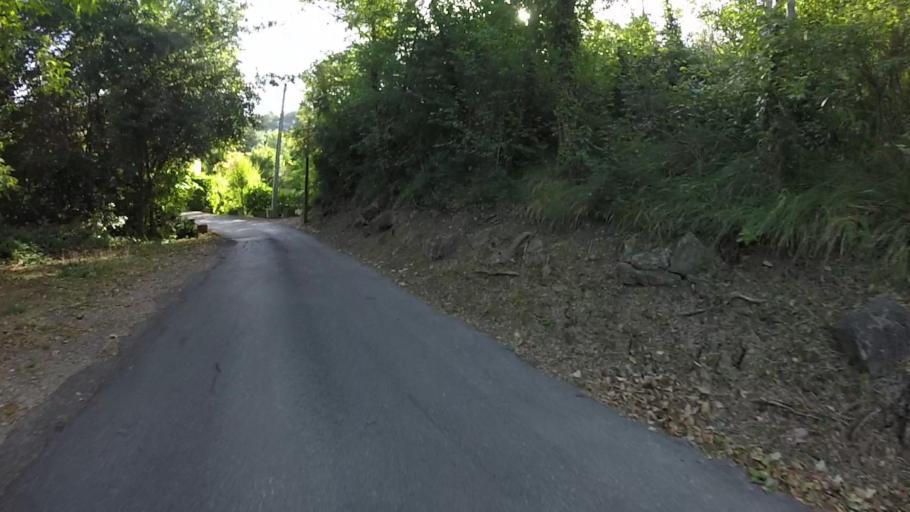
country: FR
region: Provence-Alpes-Cote d'Azur
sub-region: Departement des Alpes-Maritimes
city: Chateauneuf-Grasse
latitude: 43.6665
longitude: 6.9909
